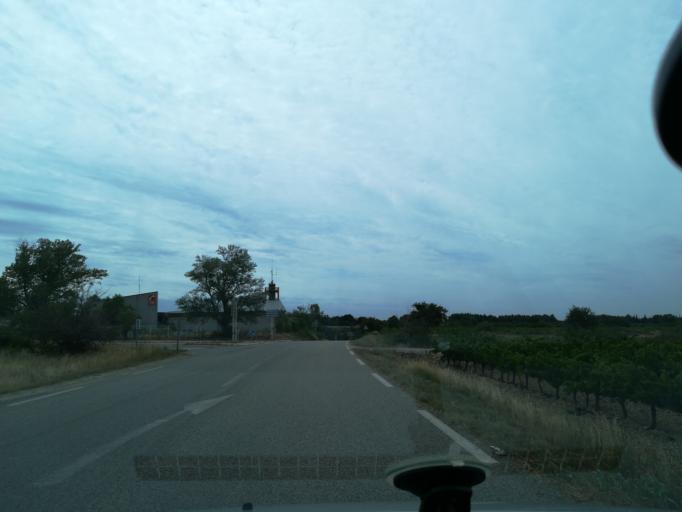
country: FR
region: Languedoc-Roussillon
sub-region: Departement du Gard
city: Remoulins
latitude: 43.9346
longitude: 4.5937
